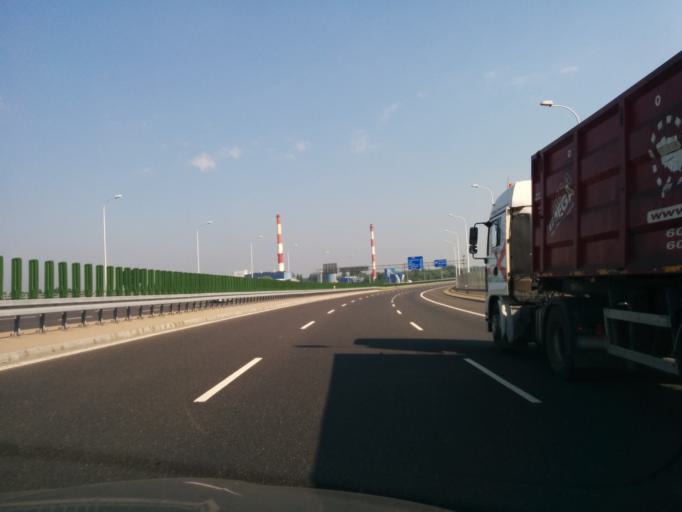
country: PL
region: Silesian Voivodeship
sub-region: Gliwice
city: Gliwice
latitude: 50.2866
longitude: 18.7156
